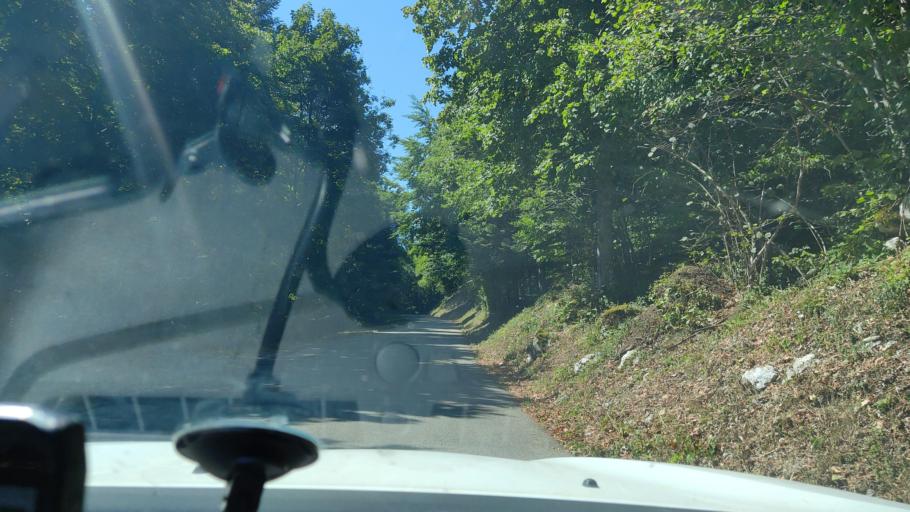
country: FR
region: Rhone-Alpes
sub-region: Departement de la Savoie
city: Le Bourget-du-Lac
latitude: 45.6625
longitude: 5.8365
